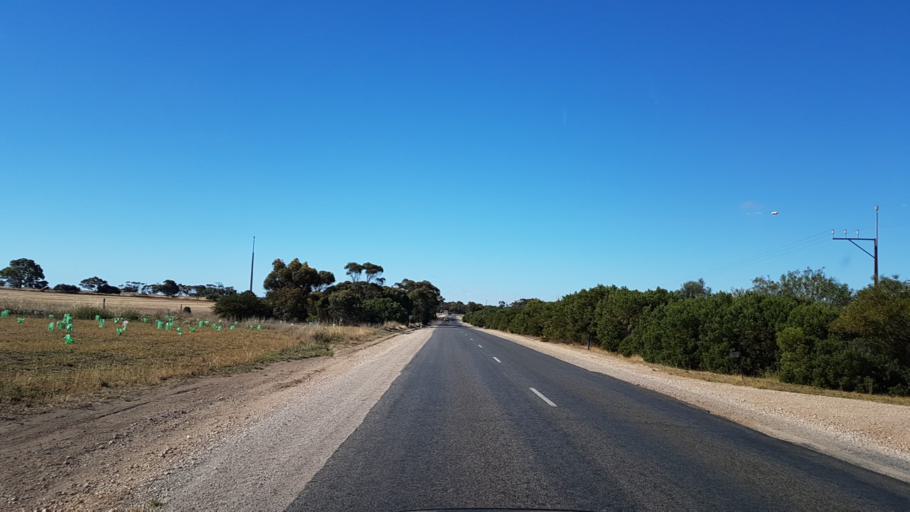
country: AU
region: South Australia
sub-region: Yorke Peninsula
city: Port Victoria
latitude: -34.7841
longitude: 137.5914
